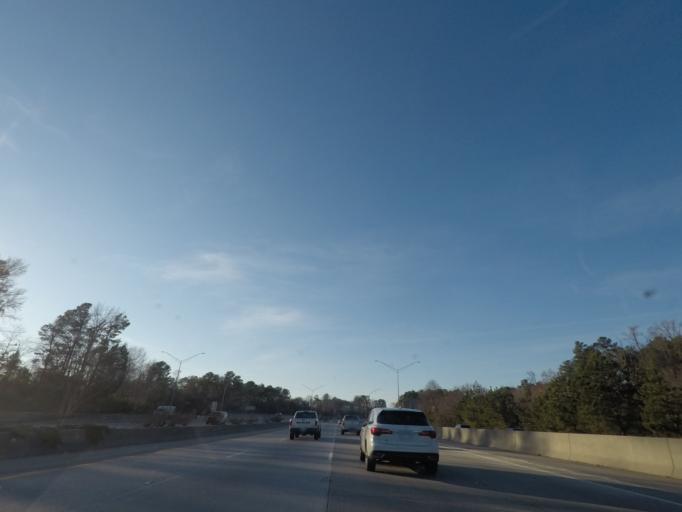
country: US
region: North Carolina
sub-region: Durham County
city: Durham
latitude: 36.0220
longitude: -78.9101
